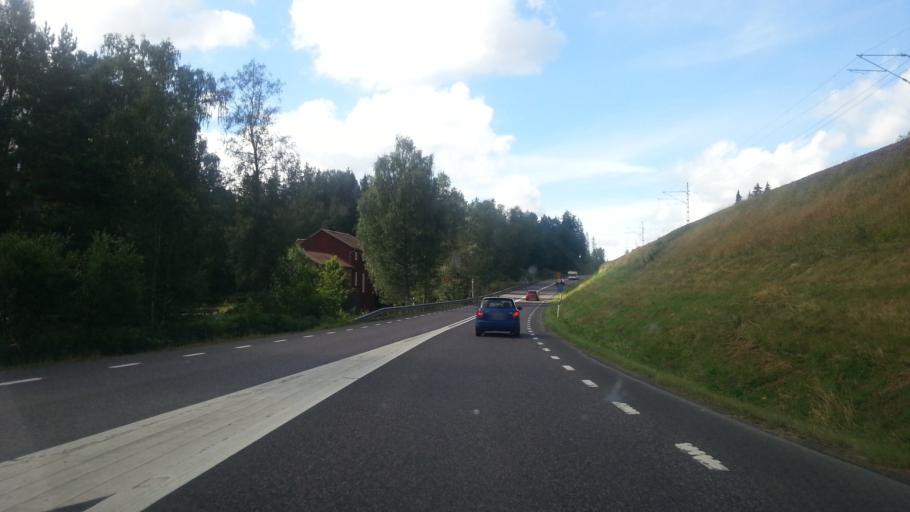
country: SE
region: Dalarna
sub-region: Ludvika Kommun
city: Ludvika
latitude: 60.1025
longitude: 15.0984
